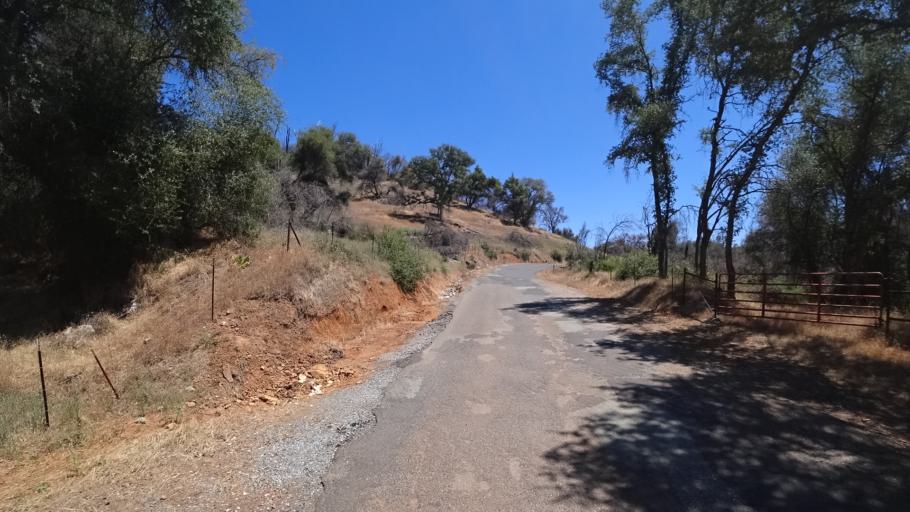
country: US
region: California
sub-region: Calaveras County
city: San Andreas
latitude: 38.2851
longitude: -120.6295
